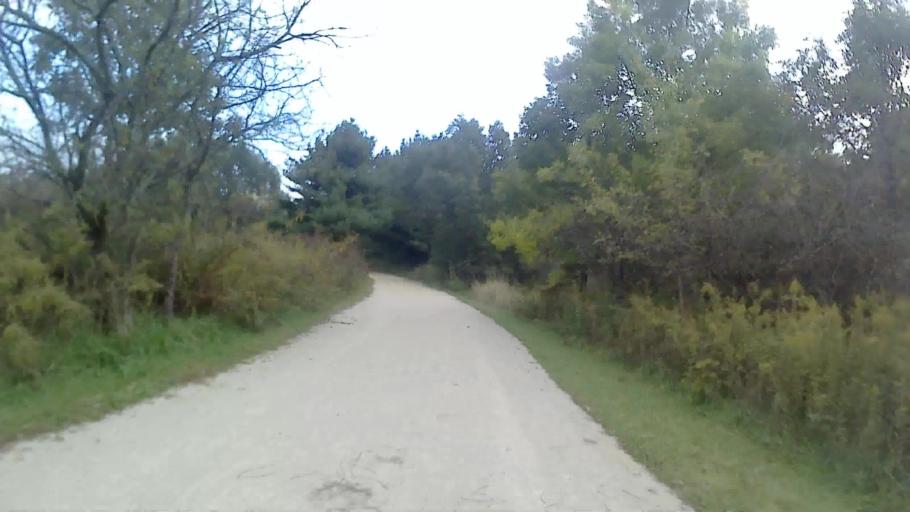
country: US
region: Illinois
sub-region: DuPage County
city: Naperville
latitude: 41.8135
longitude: -88.1456
